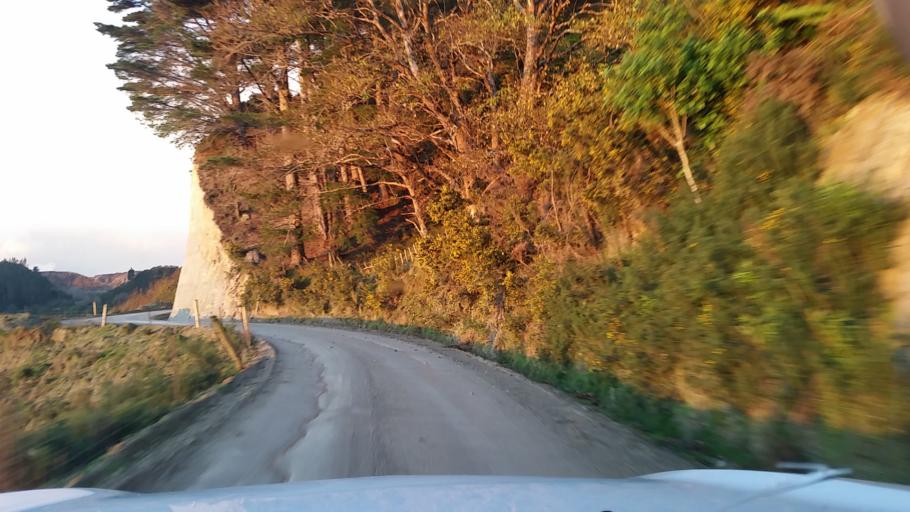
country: NZ
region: Manawatu-Wanganui
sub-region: Wanganui District
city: Wanganui
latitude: -39.7636
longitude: 174.8762
